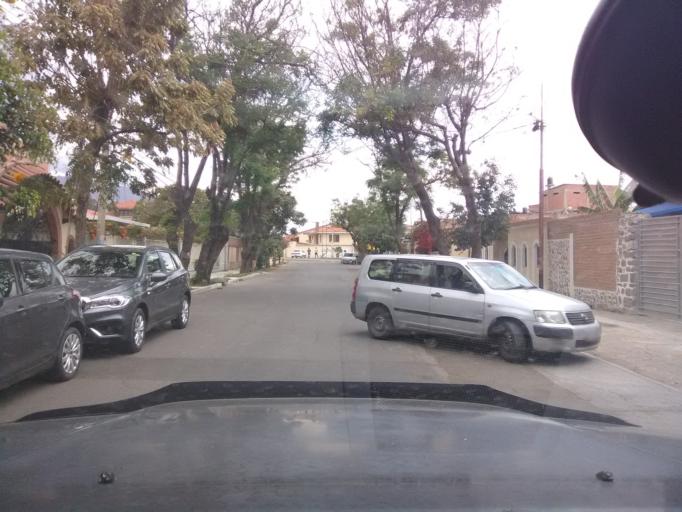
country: BO
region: Cochabamba
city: Cochabamba
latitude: -17.3648
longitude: -66.1729
